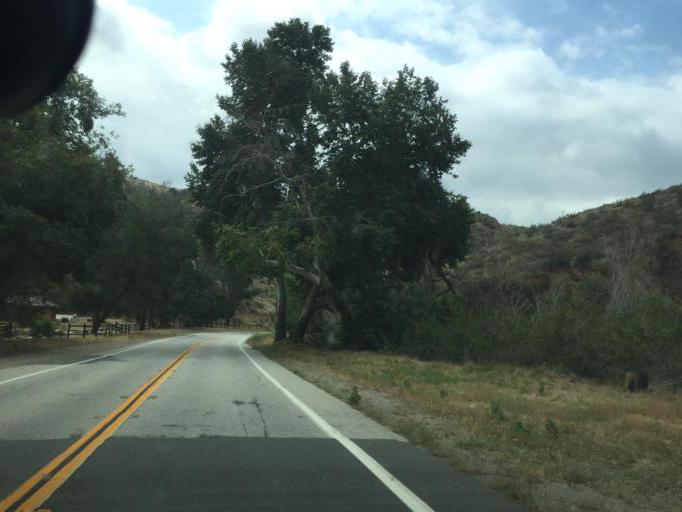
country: US
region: California
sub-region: Los Angeles County
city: Green Valley
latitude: 34.5071
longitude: -118.4524
